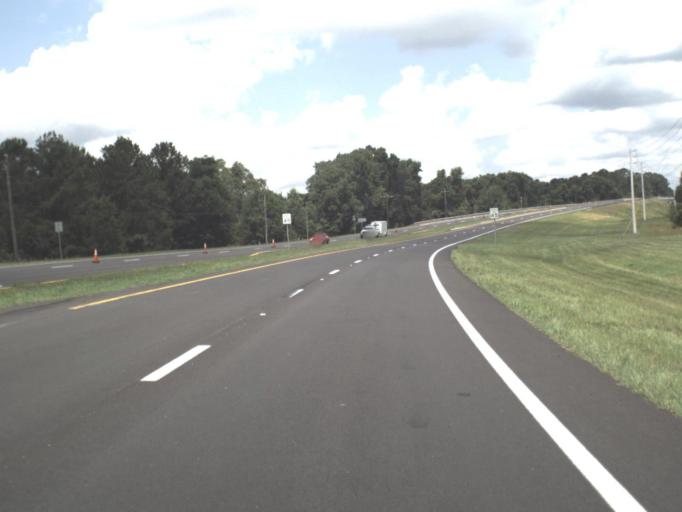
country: US
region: Florida
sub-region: Alachua County
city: Alachua
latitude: 29.7847
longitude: -82.4742
